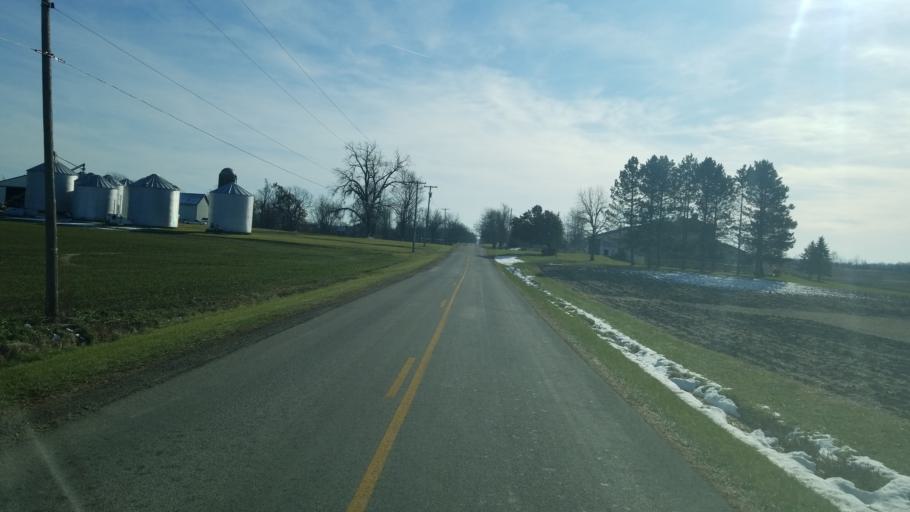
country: US
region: Ohio
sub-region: Huron County
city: New London
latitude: 41.1288
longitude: -82.3489
